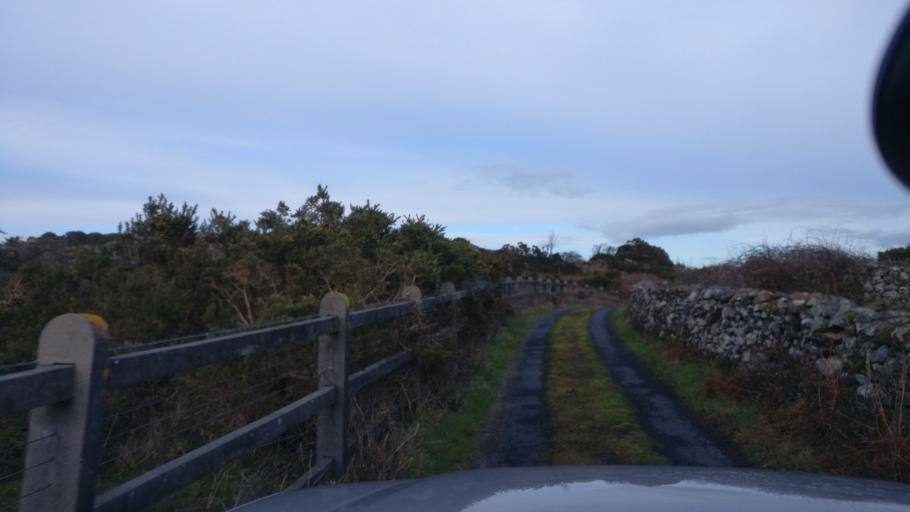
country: IE
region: Connaught
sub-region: County Galway
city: Oughterard
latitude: 53.5239
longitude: -9.3871
